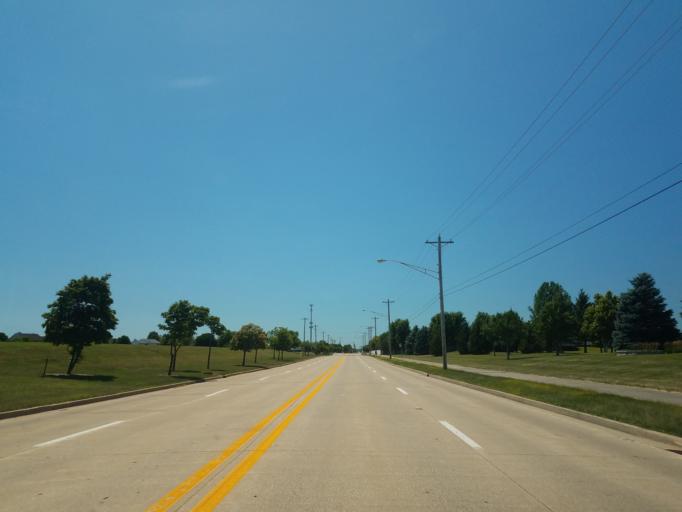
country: US
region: Illinois
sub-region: McLean County
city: Normal
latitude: 40.5027
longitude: -88.9182
